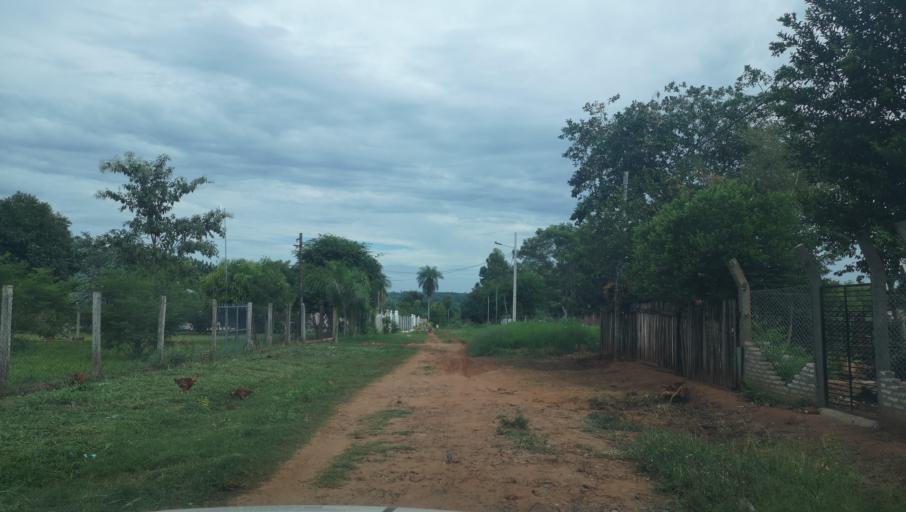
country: PY
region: San Pedro
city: Capiibary
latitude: -24.7262
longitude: -56.0227
